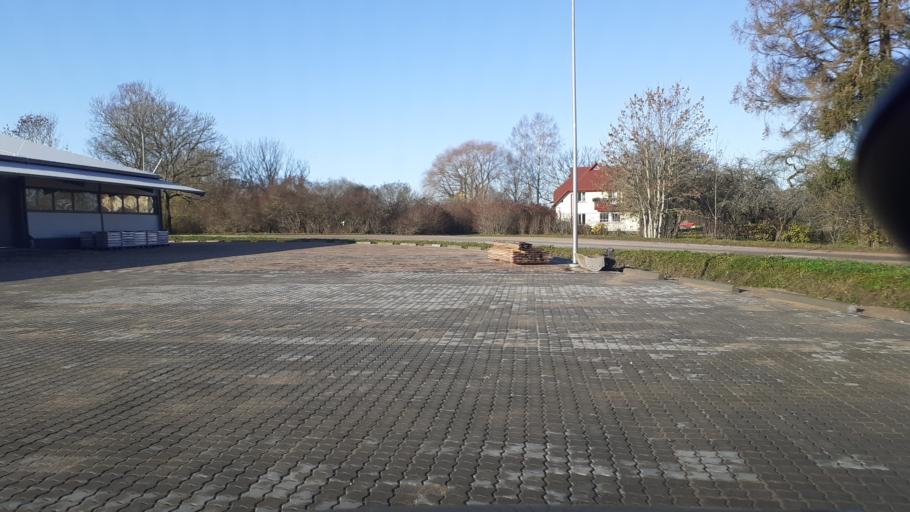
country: LV
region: Kuldigas Rajons
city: Kuldiga
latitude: 57.0003
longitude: 21.8857
